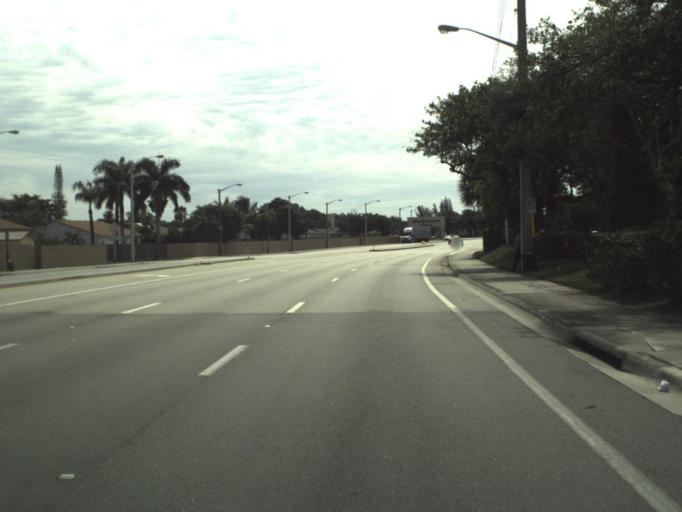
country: US
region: Florida
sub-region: Palm Beach County
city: Mangonia Park
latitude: 26.7829
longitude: -80.0908
